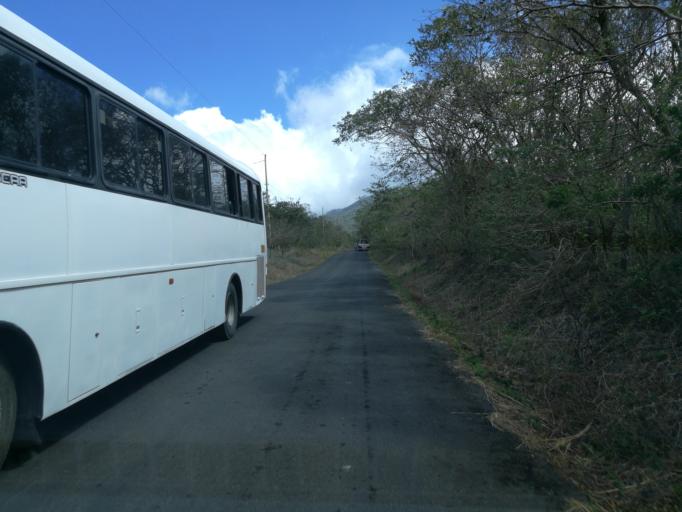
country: CR
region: Guanacaste
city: Liberia
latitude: 10.7686
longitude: -85.3514
